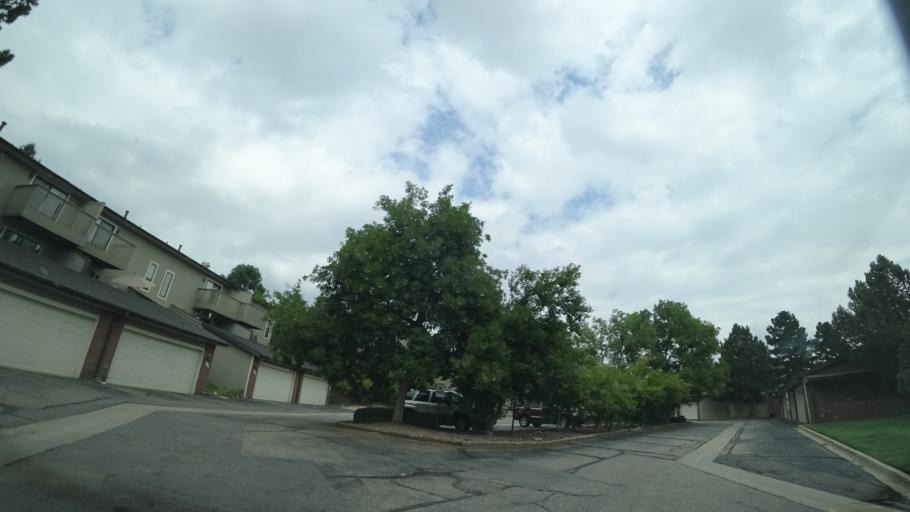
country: US
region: Colorado
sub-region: Jefferson County
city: West Pleasant View
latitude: 39.7140
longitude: -105.1640
